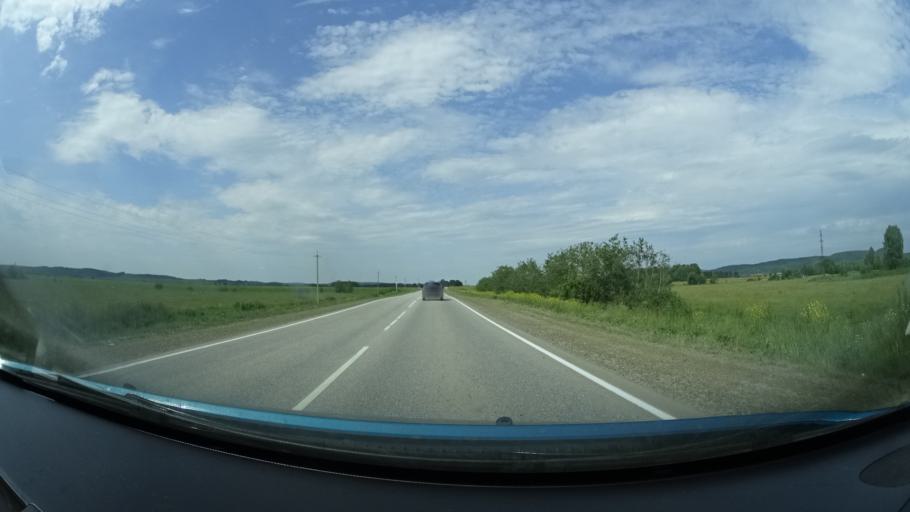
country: RU
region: Perm
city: Barda
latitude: 57.0572
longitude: 55.5431
